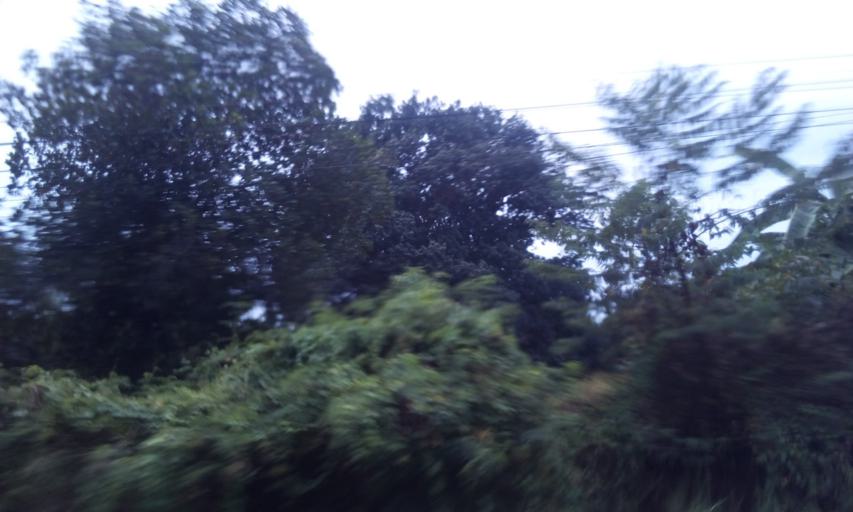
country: TH
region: Trat
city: Laem Ngop
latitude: 12.2561
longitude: 102.2872
